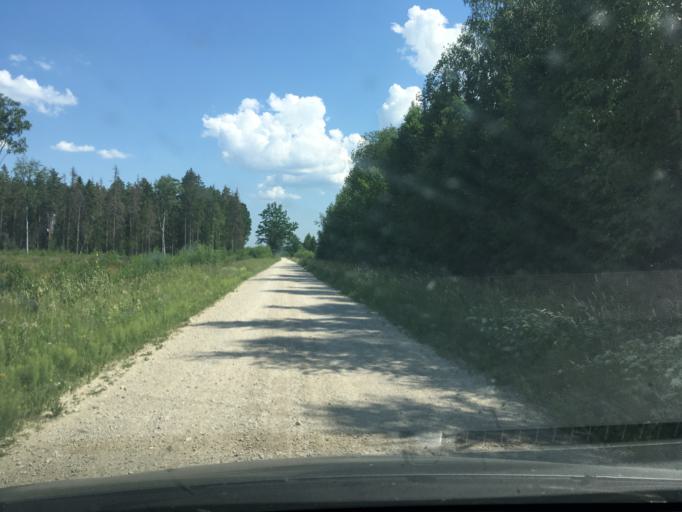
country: EE
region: Raplamaa
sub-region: Maerjamaa vald
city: Marjamaa
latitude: 58.8093
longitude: 24.4528
